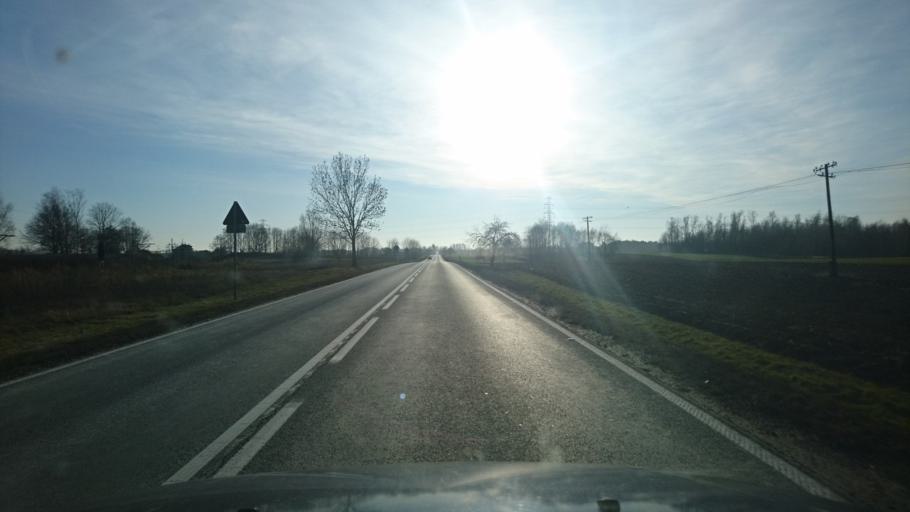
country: PL
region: Opole Voivodeship
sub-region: Powiat oleski
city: Dalachow
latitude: 51.0623
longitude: 18.6000
